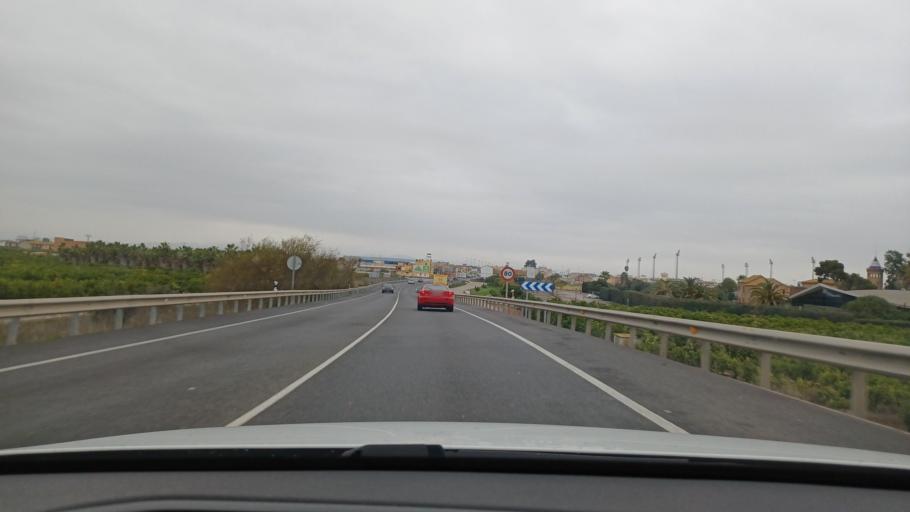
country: ES
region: Valencia
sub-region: Provincia de Castello
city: Alquerias del Nino Perdido
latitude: 39.8899
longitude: -0.1262
